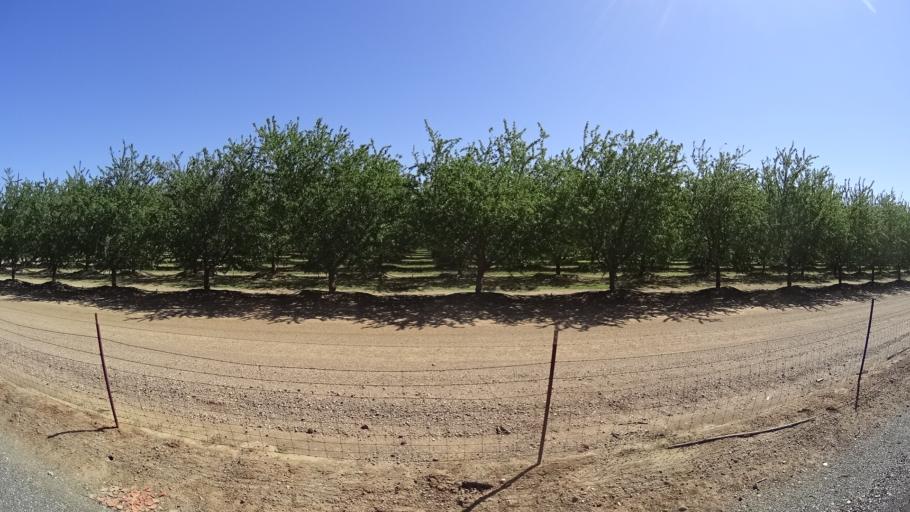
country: US
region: California
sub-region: Glenn County
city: Orland
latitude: 39.6676
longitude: -122.2531
